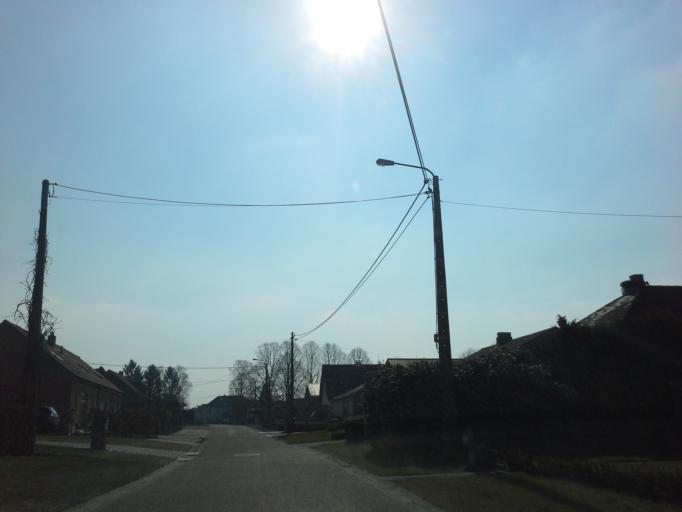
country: BE
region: Flanders
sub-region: Provincie Antwerpen
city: Meerhout
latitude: 51.1362
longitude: 5.0676
